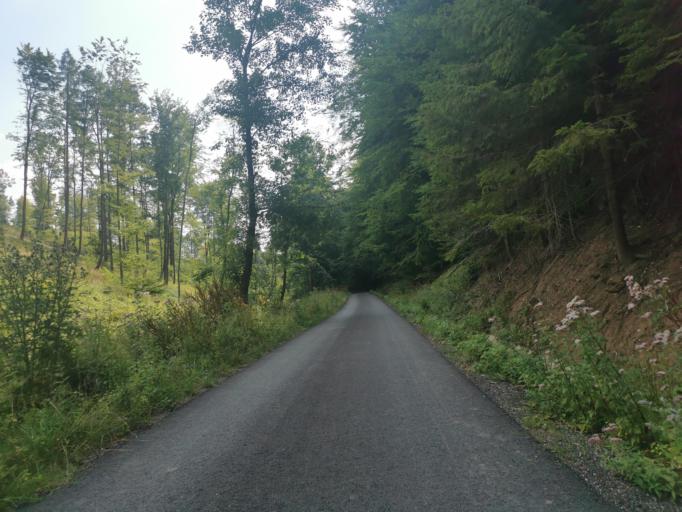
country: SK
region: Trenciansky
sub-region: Okres Myjava
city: Myjava
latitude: 48.8370
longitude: 17.6086
